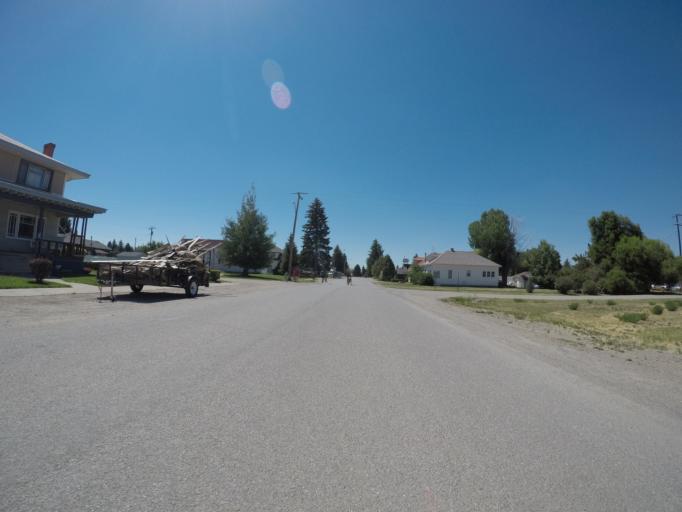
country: US
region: Idaho
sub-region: Bear Lake County
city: Montpelier
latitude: 42.0849
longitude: -110.9564
